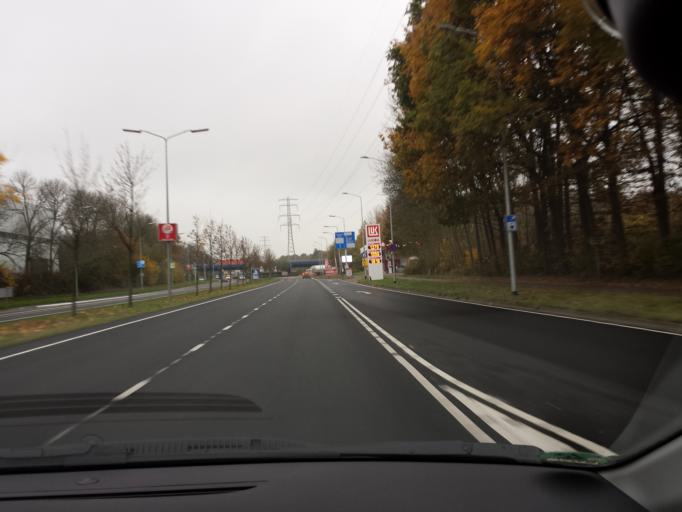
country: NL
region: Limburg
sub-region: Gemeente Simpelveld
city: Simpelveld
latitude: 50.8590
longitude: 6.0029
